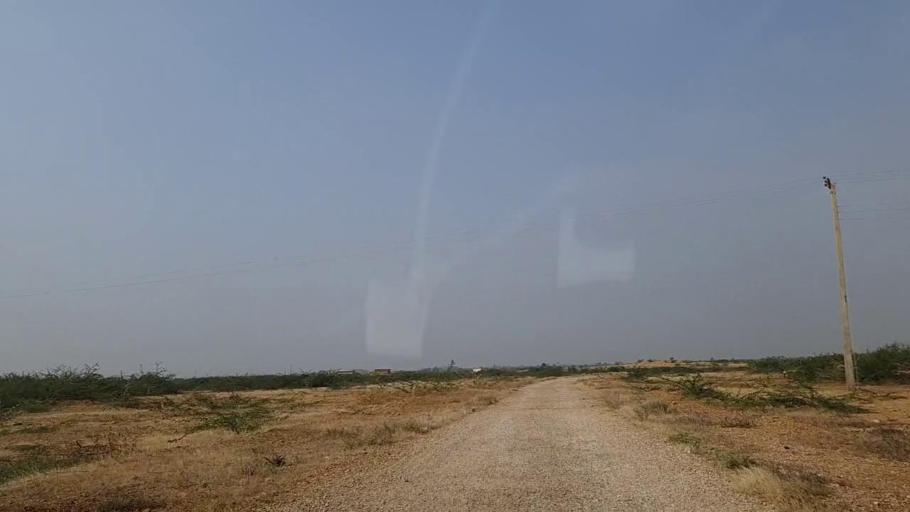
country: PK
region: Sindh
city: Thatta
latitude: 24.7207
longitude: 67.8294
